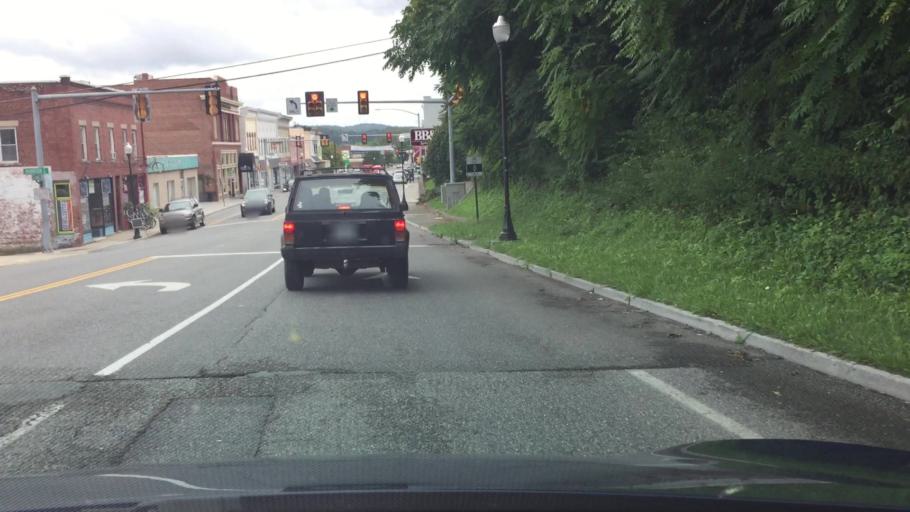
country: US
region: Virginia
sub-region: City of Radford
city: Radford
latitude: 37.1407
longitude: -80.5594
